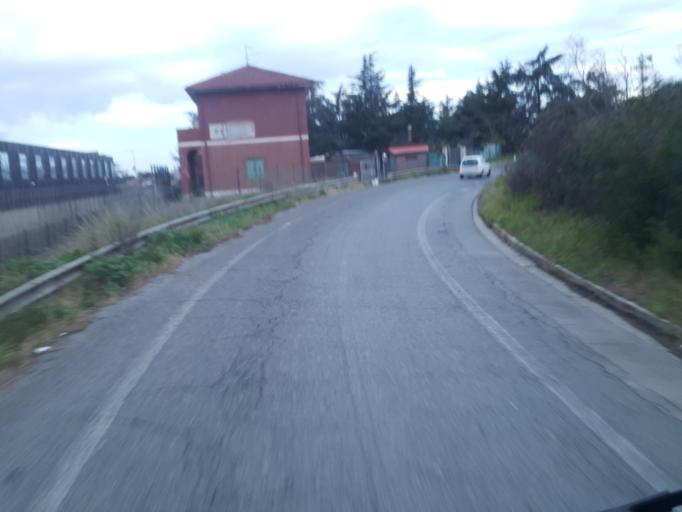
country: IT
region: Latium
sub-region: Citta metropolitana di Roma Capitale
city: Area Produttiva
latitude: 41.6755
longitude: 12.5012
